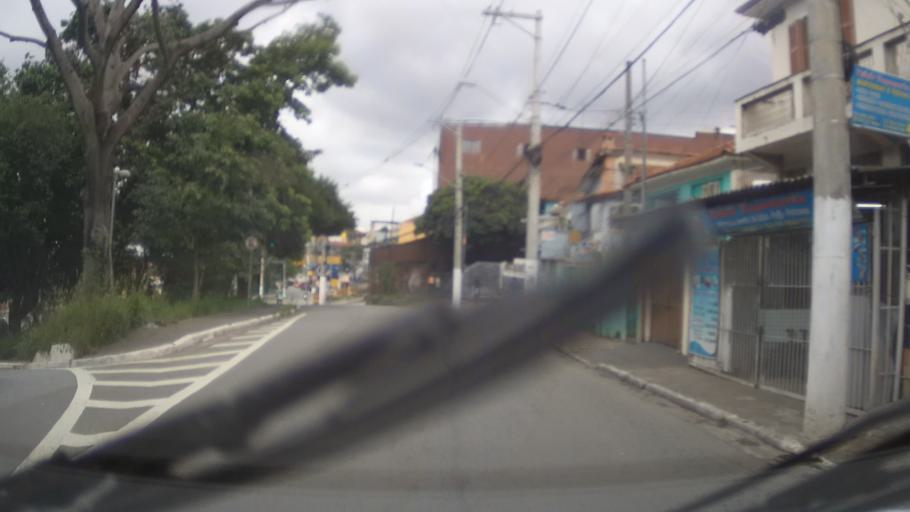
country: BR
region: Sao Paulo
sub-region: Guarulhos
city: Guarulhos
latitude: -23.4684
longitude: -46.5937
